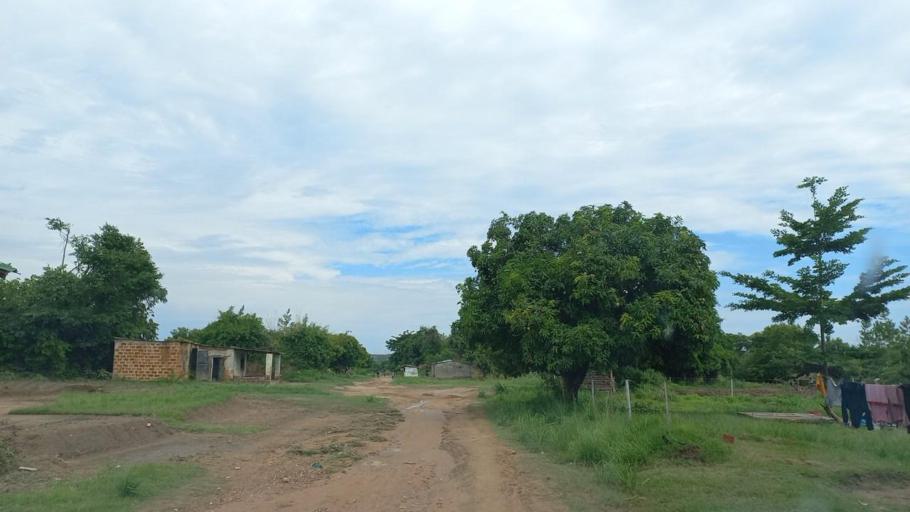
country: ZM
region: Copperbelt
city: Kitwe
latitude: -12.8655
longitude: 28.3347
